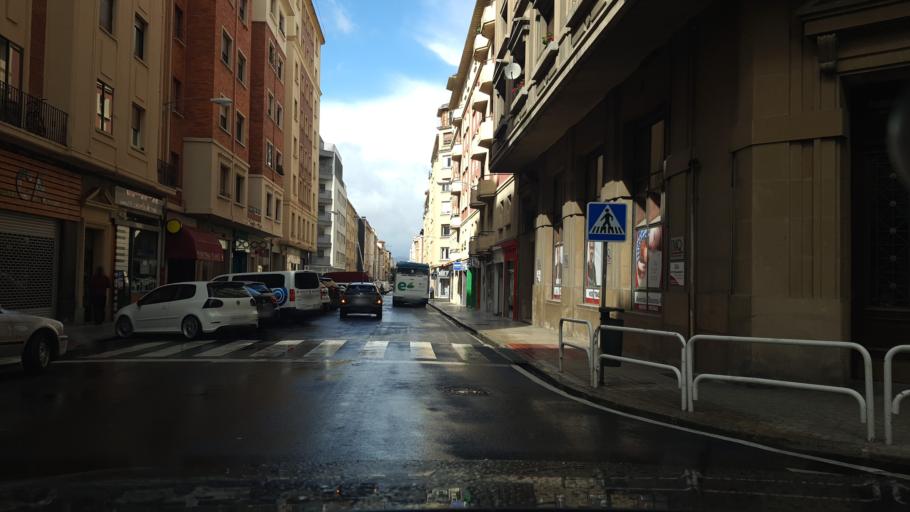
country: ES
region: Navarre
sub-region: Provincia de Navarra
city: Segundo Ensanche
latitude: 42.8096
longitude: -1.6366
